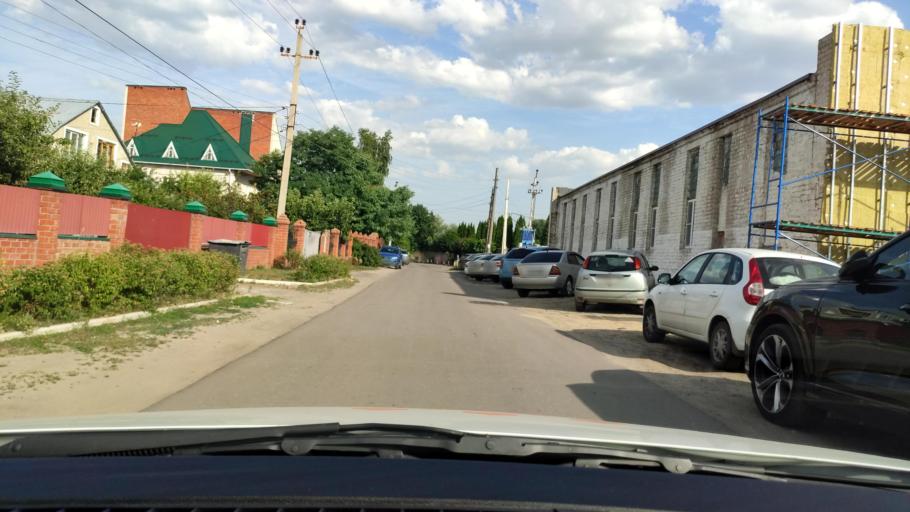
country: RU
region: Voronezj
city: Novaya Usman'
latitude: 51.6301
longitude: 39.4167
